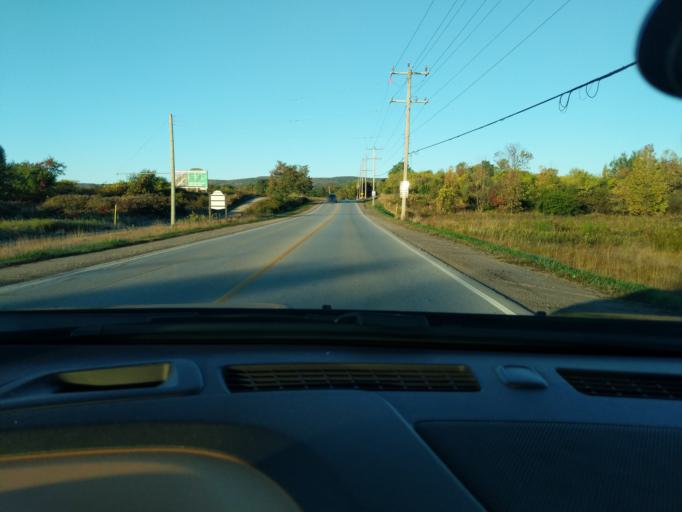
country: CA
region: Ontario
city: Collingwood
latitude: 44.4996
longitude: -80.2512
